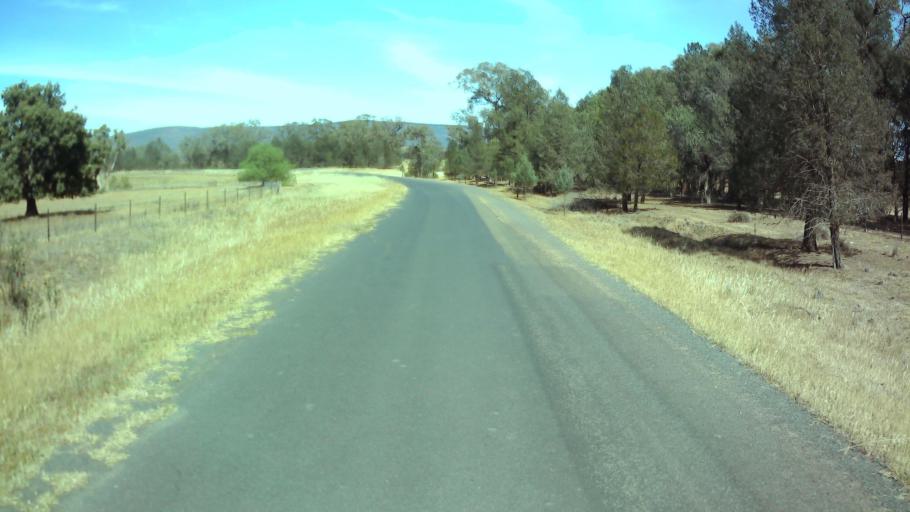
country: AU
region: New South Wales
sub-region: Weddin
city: Grenfell
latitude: -33.9316
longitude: 148.0893
